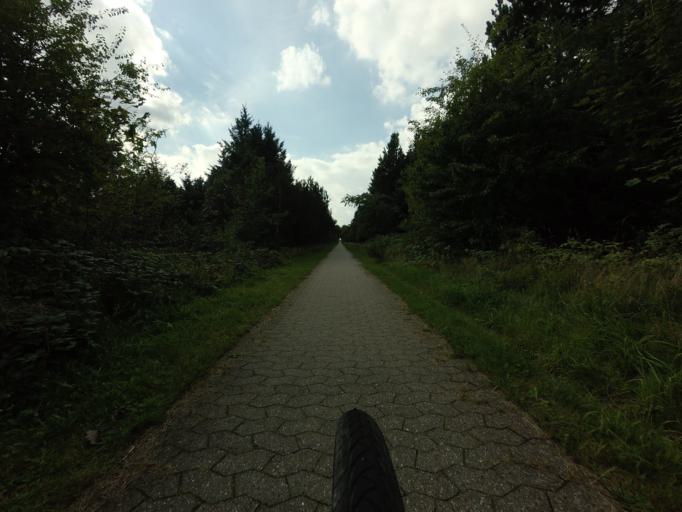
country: DK
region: Central Jutland
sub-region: Viborg Kommune
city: Karup
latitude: 56.3230
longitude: 9.2133
